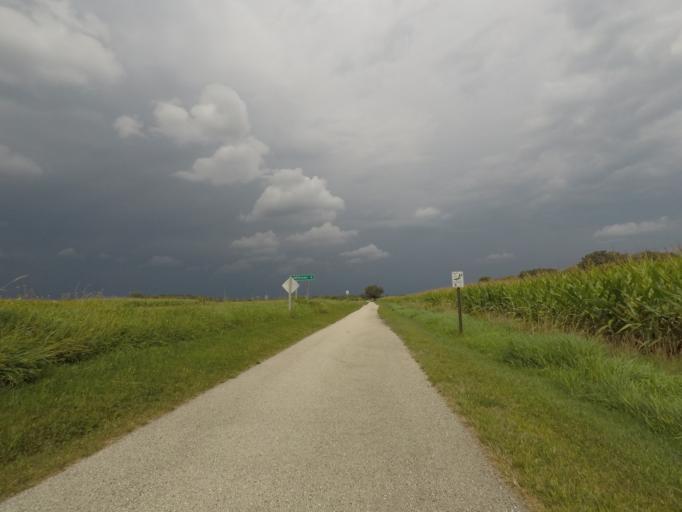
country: US
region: Wisconsin
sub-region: Jefferson County
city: Fort Atkinson
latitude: 42.9453
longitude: -88.8275
